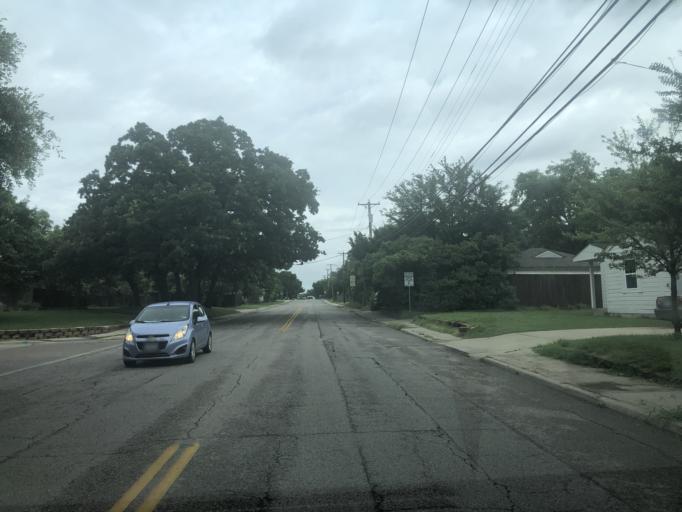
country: US
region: Texas
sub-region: Dallas County
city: Irving
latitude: 32.8028
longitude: -96.9346
